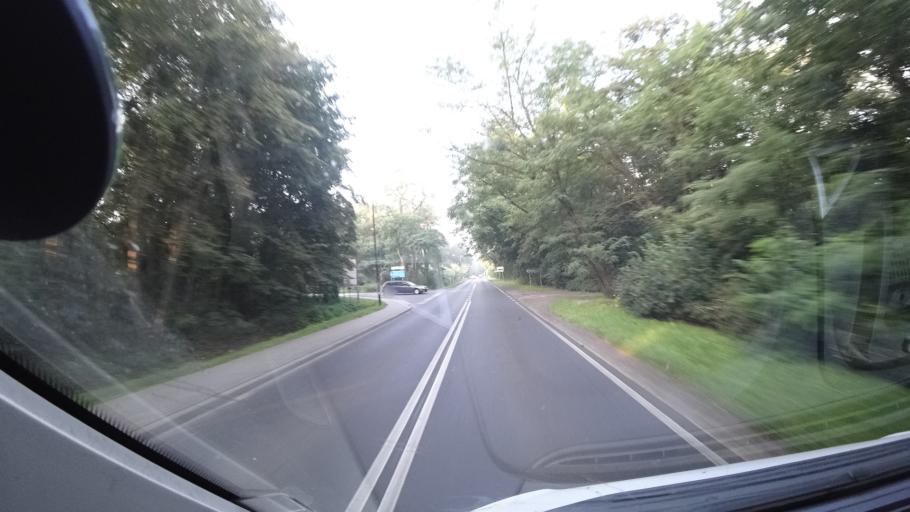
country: PL
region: Opole Voivodeship
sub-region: Powiat kedzierzynsko-kozielski
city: Slawiecice
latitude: 50.3705
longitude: 18.3176
